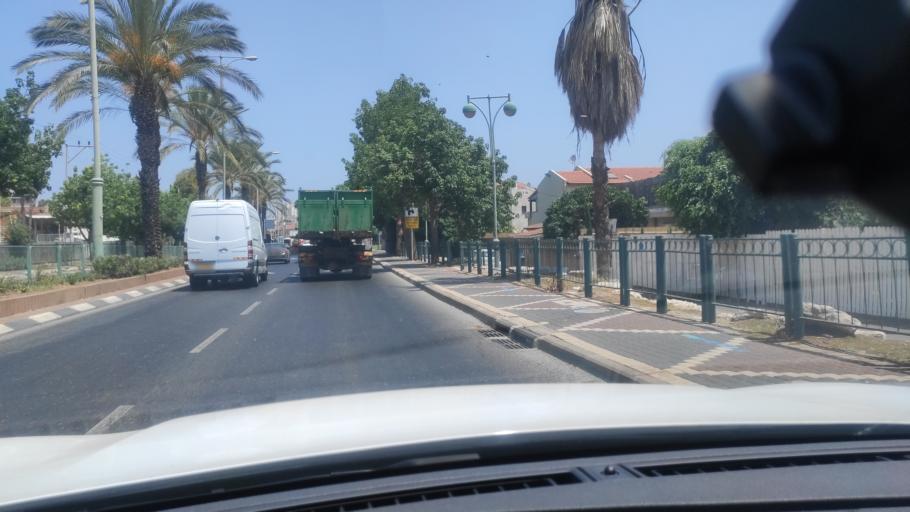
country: IL
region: Central District
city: Petah Tiqwa
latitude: 32.0947
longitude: 34.9019
